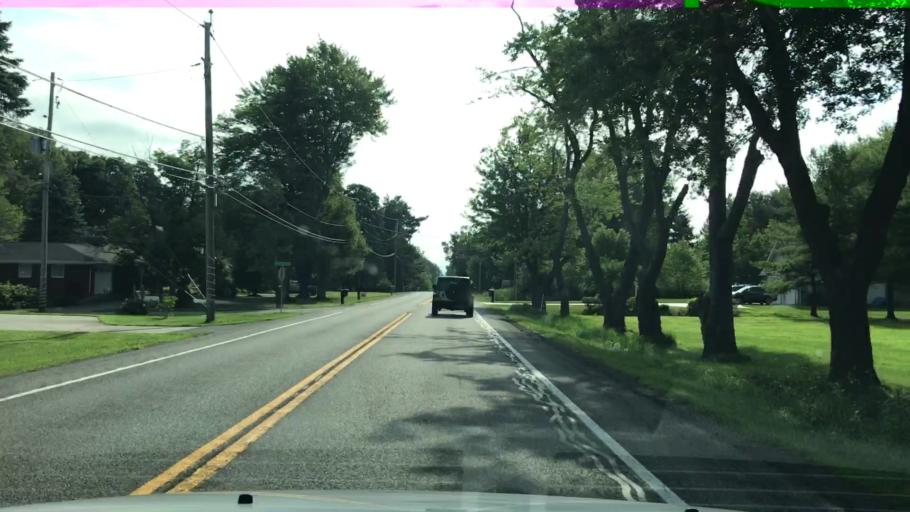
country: US
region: New York
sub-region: Erie County
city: Town Line
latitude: 42.8560
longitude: -78.5964
